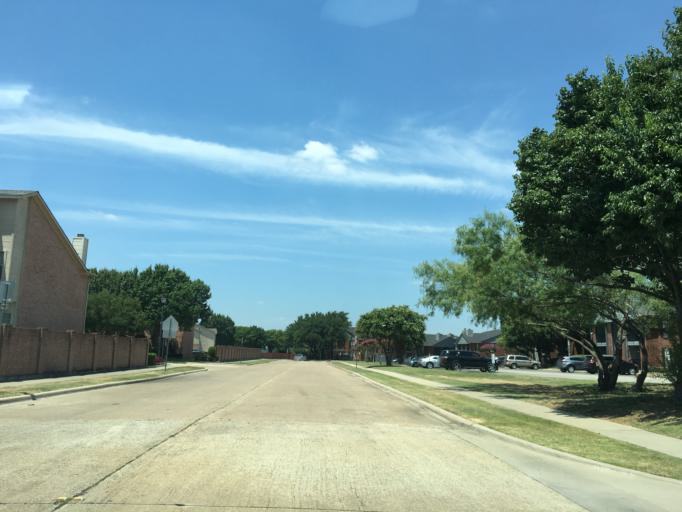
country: US
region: Texas
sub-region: Denton County
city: Lewisville
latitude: 33.0223
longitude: -96.9972
